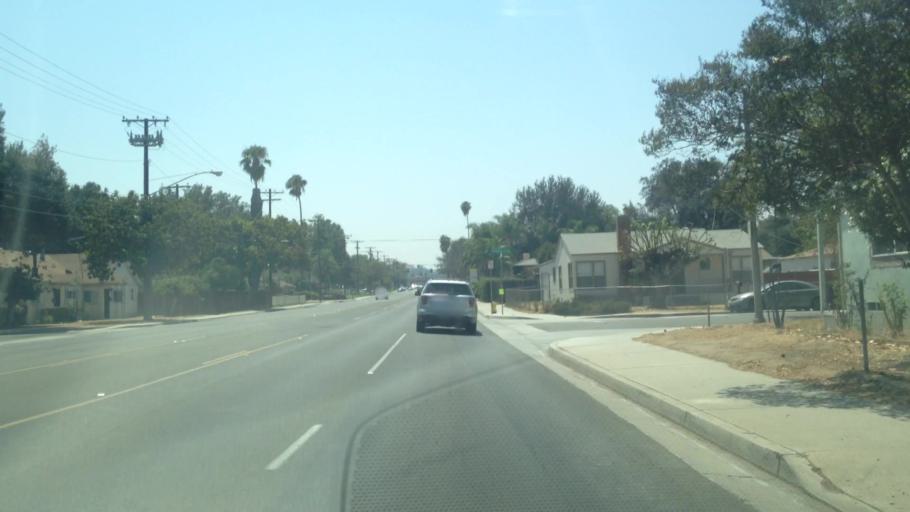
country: US
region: California
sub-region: Riverside County
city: Riverside
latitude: 33.9408
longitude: -117.4091
